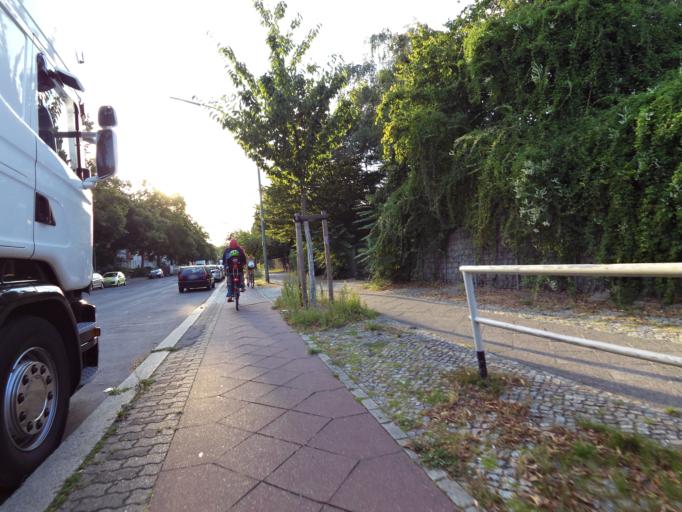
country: DE
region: Berlin
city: Schoneberg Bezirk
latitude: 52.4708
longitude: 13.3468
